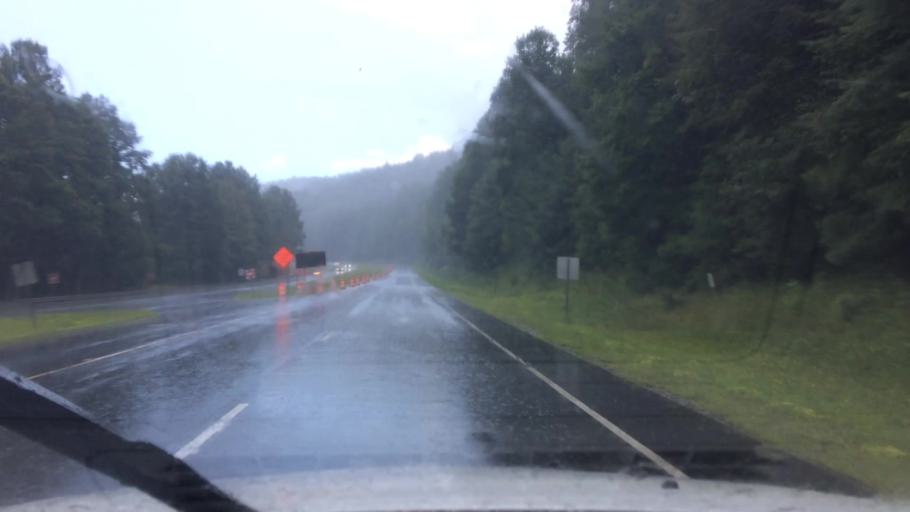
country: US
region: North Carolina
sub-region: Wilkes County
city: Millers Creek
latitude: 36.2005
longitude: -81.4318
